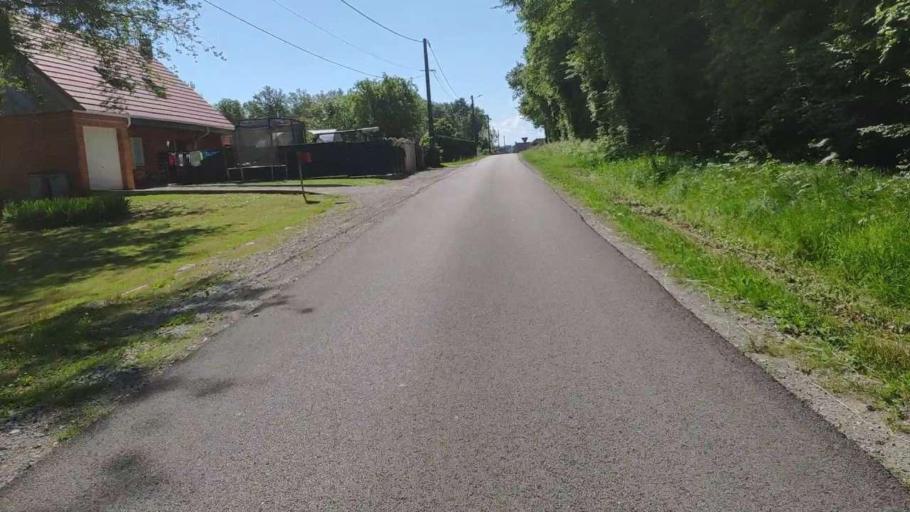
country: FR
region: Franche-Comte
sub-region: Departement du Jura
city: Bletterans
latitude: 46.7972
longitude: 5.4469
